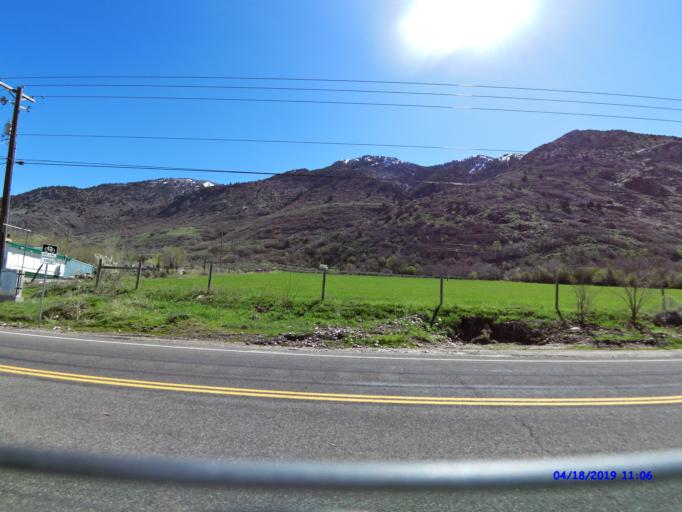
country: US
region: Utah
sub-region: Weber County
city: North Ogden
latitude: 41.2847
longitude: -111.9490
